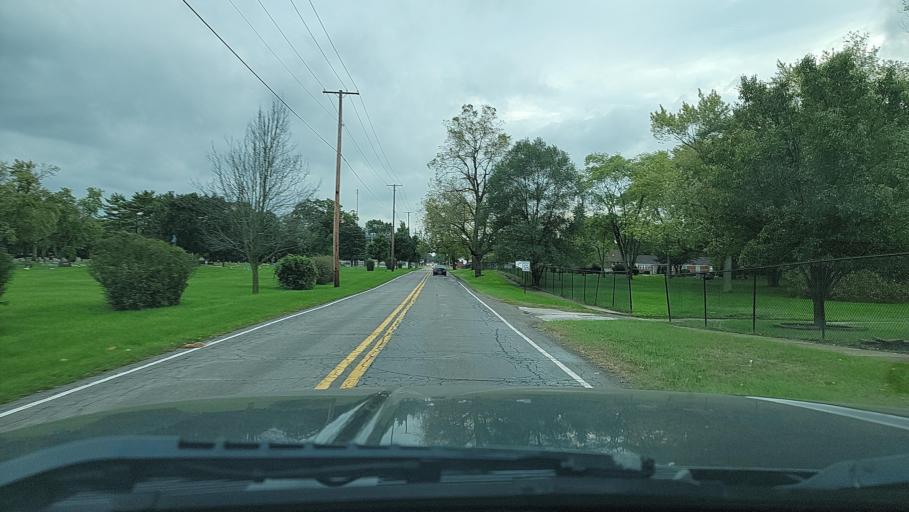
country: US
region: Indiana
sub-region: Porter County
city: Portage
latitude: 41.5744
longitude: -87.2024
